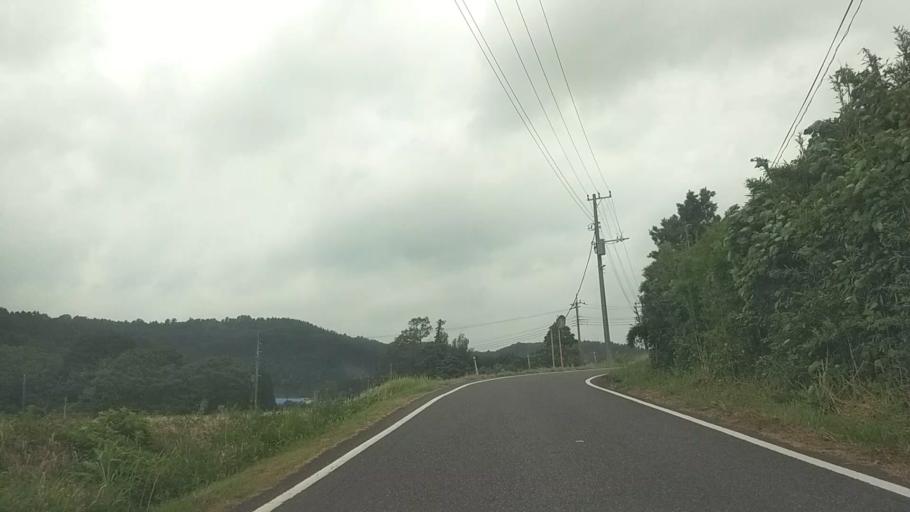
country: JP
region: Chiba
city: Kawaguchi
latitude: 35.2627
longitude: 140.0577
